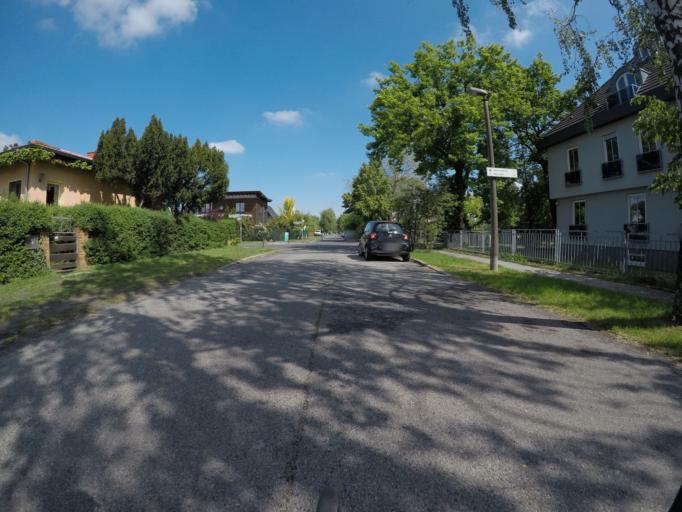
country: DE
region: Berlin
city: Biesdorf
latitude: 52.5277
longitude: 13.5505
